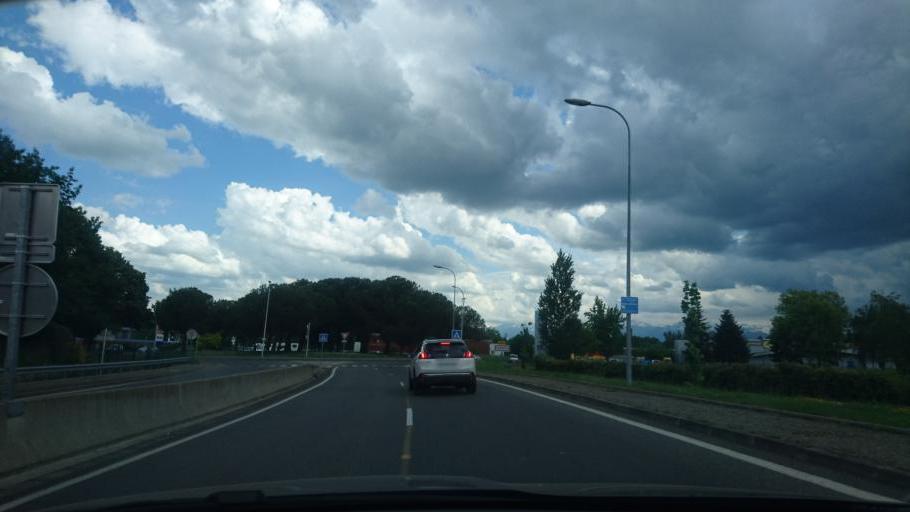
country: FR
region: Midi-Pyrenees
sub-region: Departement des Hautes-Pyrenees
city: Odos
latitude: 43.2239
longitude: 0.0456
